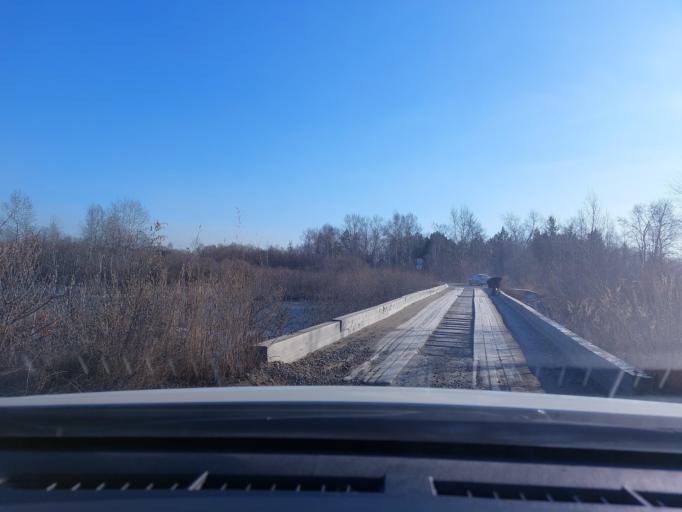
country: RU
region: Irkutsk
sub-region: Irkutskiy Rayon
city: Irkutsk
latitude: 52.3006
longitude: 104.2765
